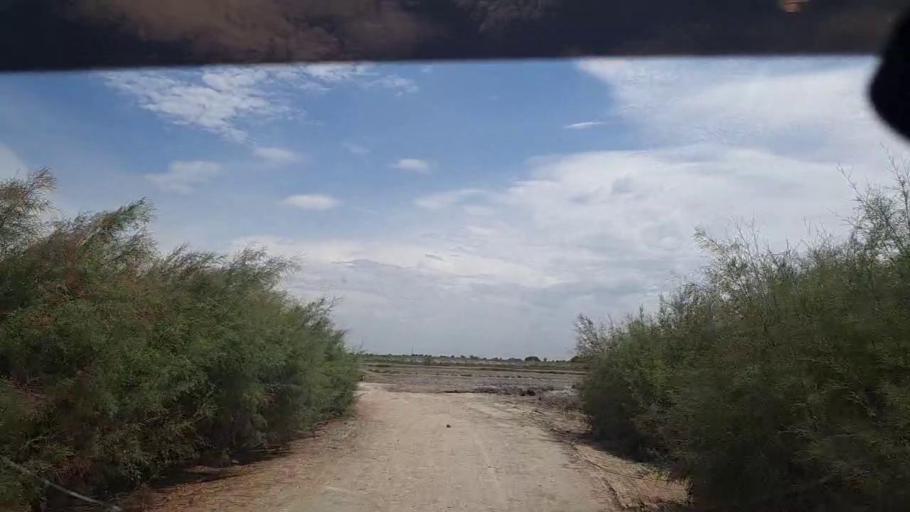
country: PK
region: Sindh
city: Ghauspur
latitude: 28.1439
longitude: 68.9780
